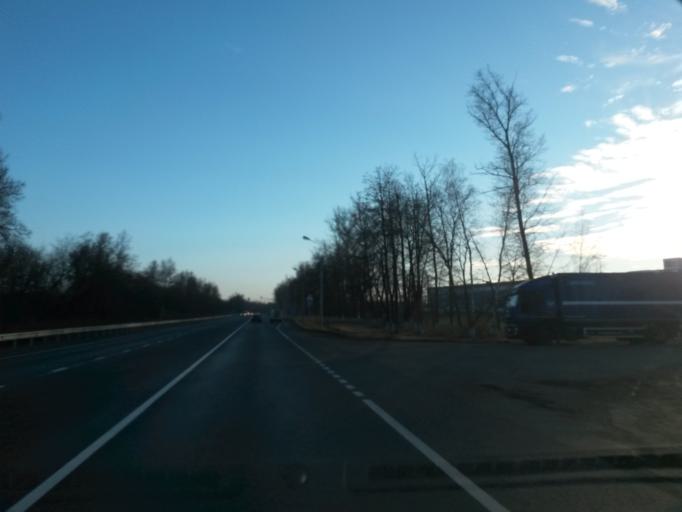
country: RU
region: Moskovskaya
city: L'vovskiy
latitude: 55.3075
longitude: 37.5288
